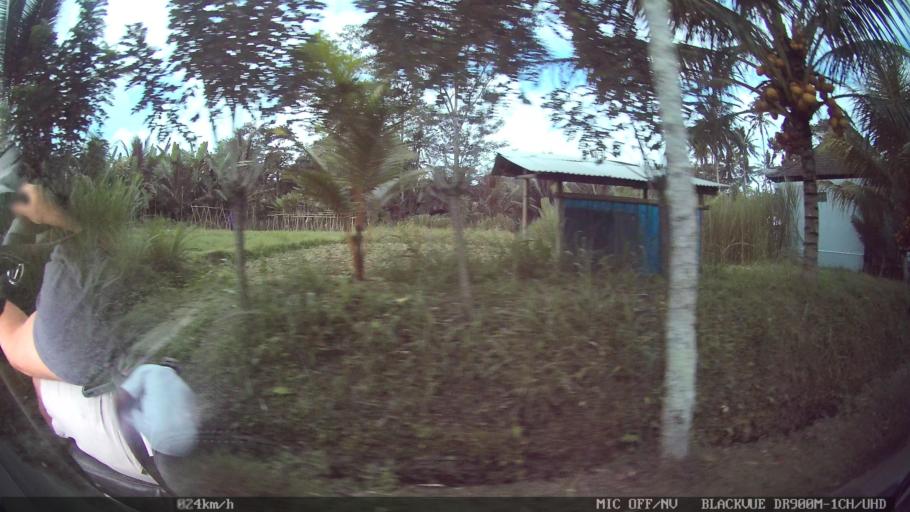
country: ID
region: Bali
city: Banjar Petak
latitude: -8.4453
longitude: 115.3224
